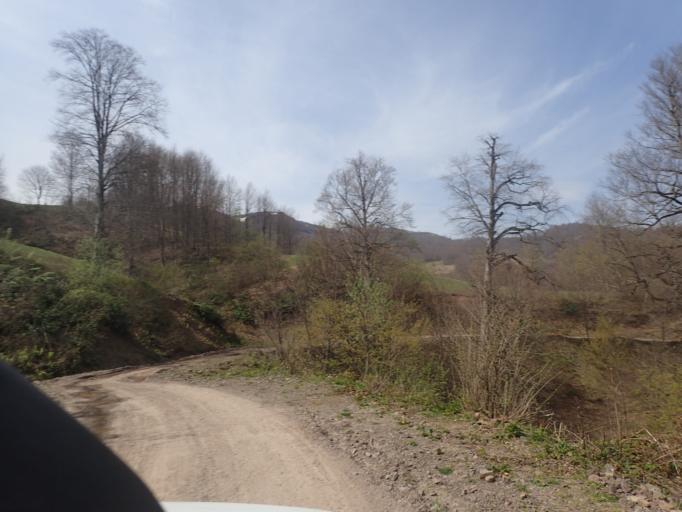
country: TR
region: Ordu
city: Aybasti
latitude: 40.6893
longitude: 37.2680
